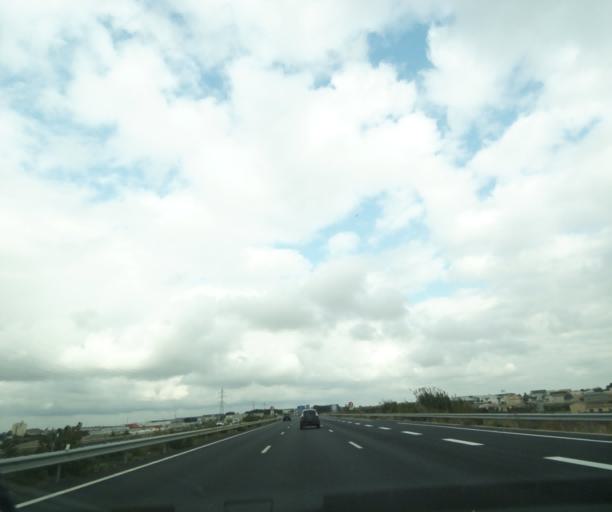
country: FR
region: Languedoc-Roussillon
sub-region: Departement de l'Herault
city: Villeneuve-les-Beziers
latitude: 43.3277
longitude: 3.2759
